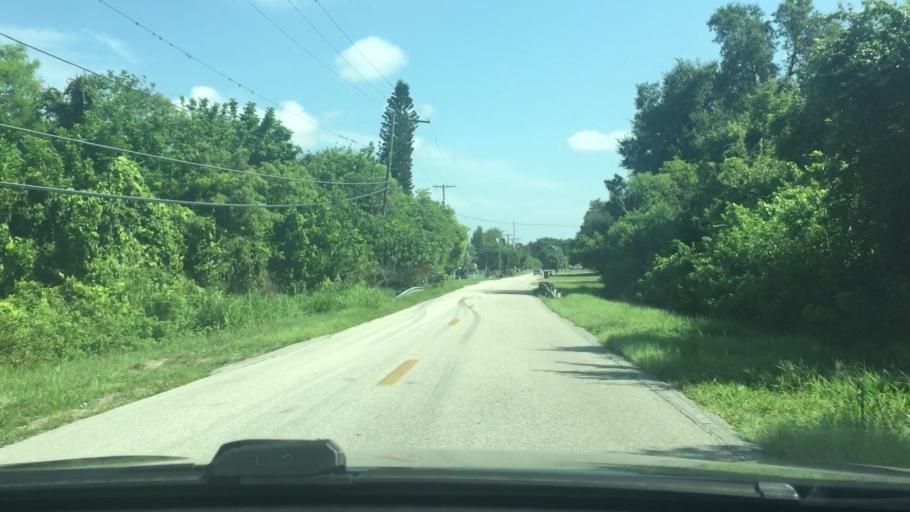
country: US
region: Florida
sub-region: Hillsborough County
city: Ruskin
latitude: 27.7018
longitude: -82.4436
